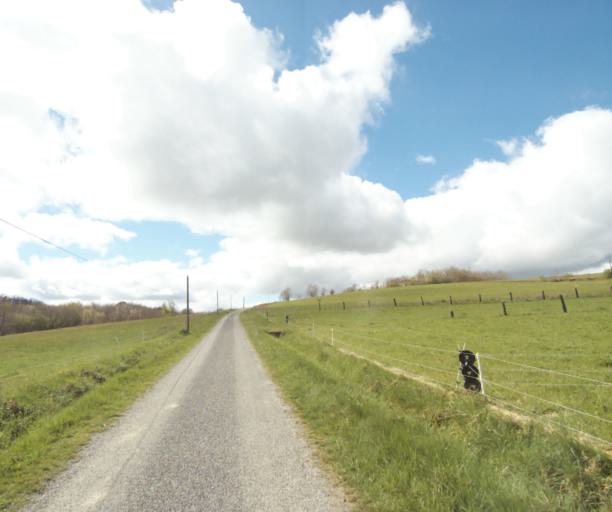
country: FR
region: Midi-Pyrenees
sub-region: Departement de l'Ariege
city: Saverdun
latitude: 43.1905
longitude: 1.5816
